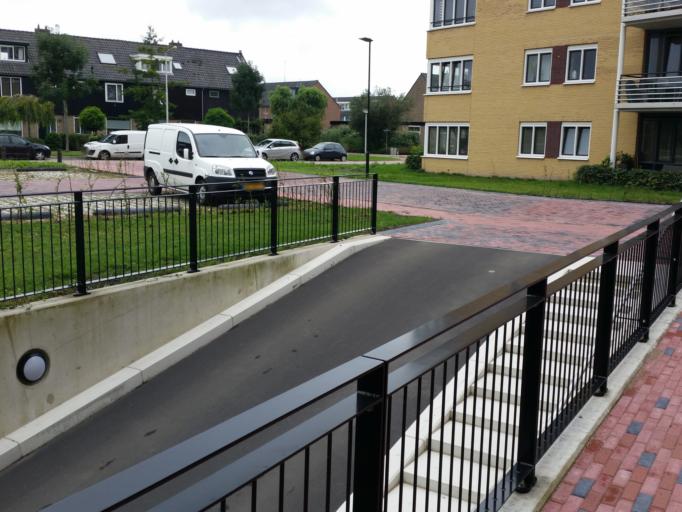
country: NL
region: North Holland
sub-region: Gemeente Ouder-Amstel
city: Ouderkerk aan de Amstel
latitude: 52.2999
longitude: 4.9176
